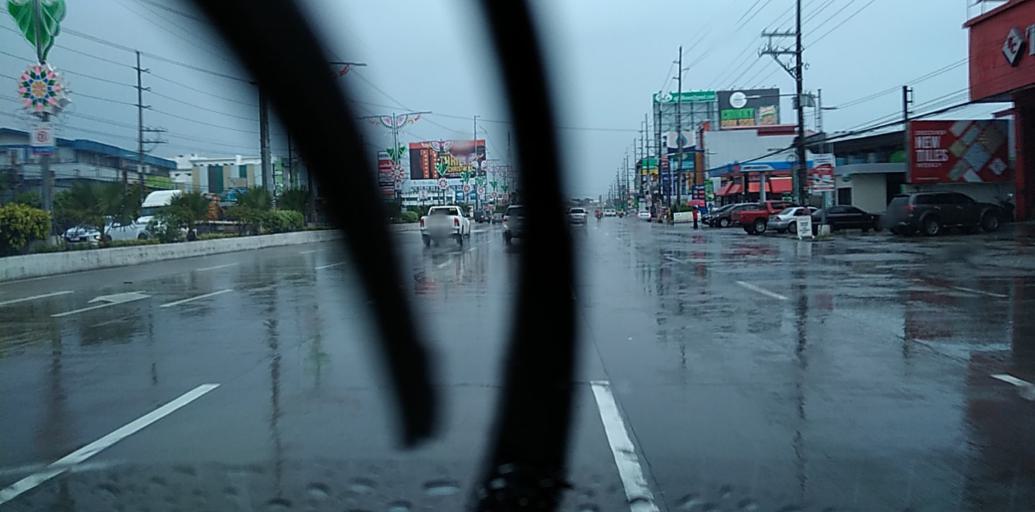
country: PH
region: Central Luzon
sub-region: Province of Pampanga
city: San Fernando
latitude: 15.0402
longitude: 120.6825
